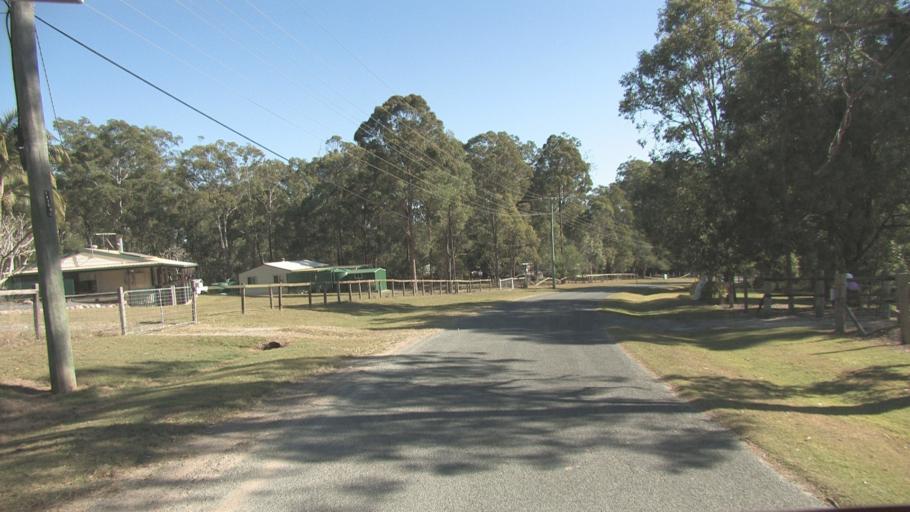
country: AU
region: Queensland
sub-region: Logan
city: Chambers Flat
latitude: -27.7954
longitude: 153.1454
